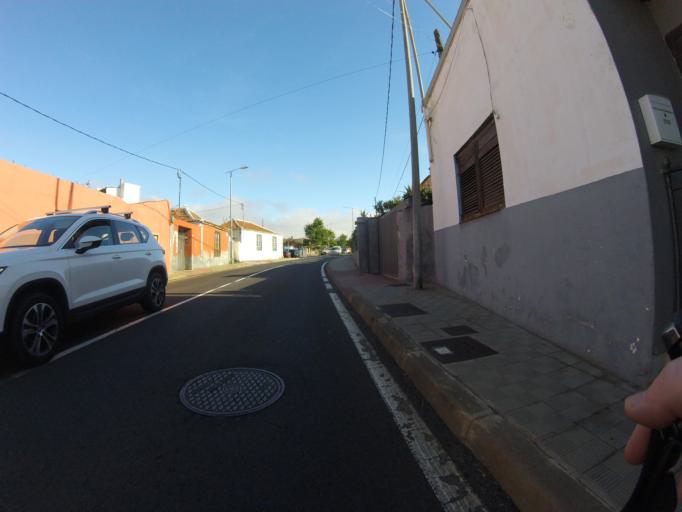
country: ES
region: Canary Islands
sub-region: Provincia de Santa Cruz de Tenerife
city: La Laguna
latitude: 28.4624
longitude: -16.3160
